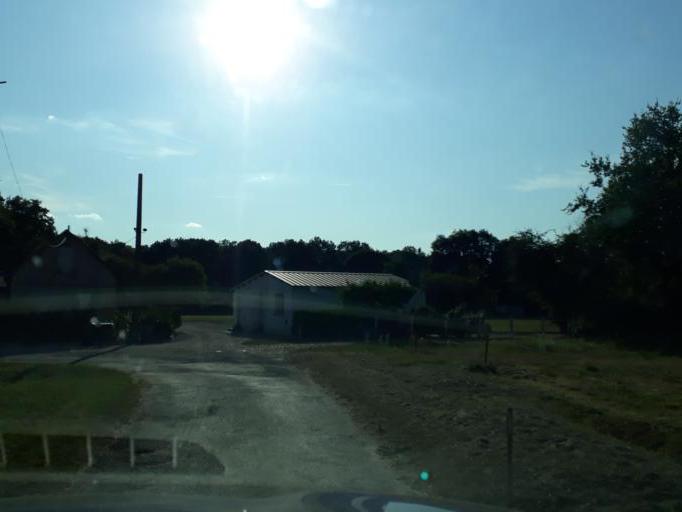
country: FR
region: Centre
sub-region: Departement du Loiret
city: Chaingy
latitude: 47.9089
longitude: 1.7518
